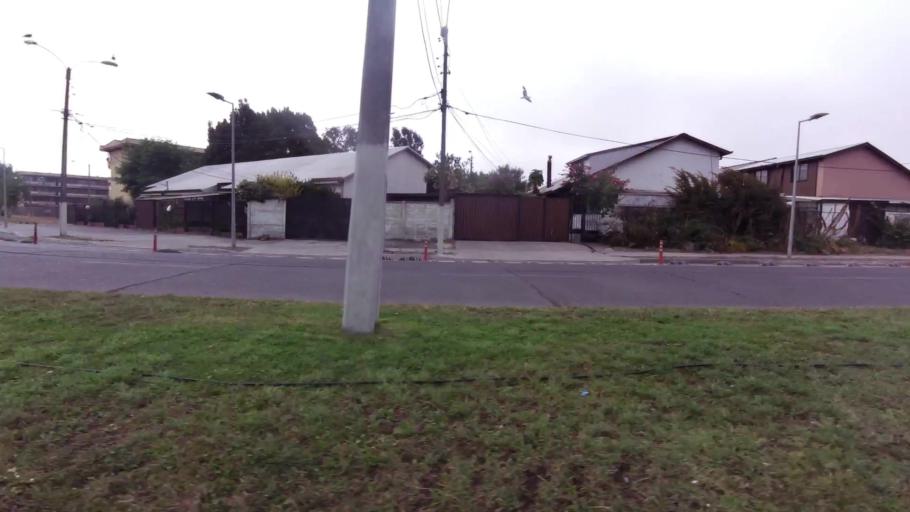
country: CL
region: Biobio
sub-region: Provincia de Concepcion
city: Concepcion
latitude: -36.7902
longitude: -73.0911
